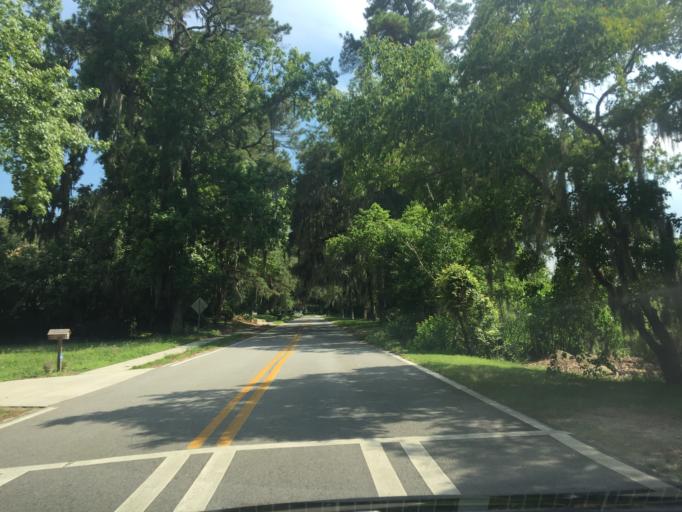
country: US
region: Georgia
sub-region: Chatham County
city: Isle of Hope
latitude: 31.9896
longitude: -81.1027
